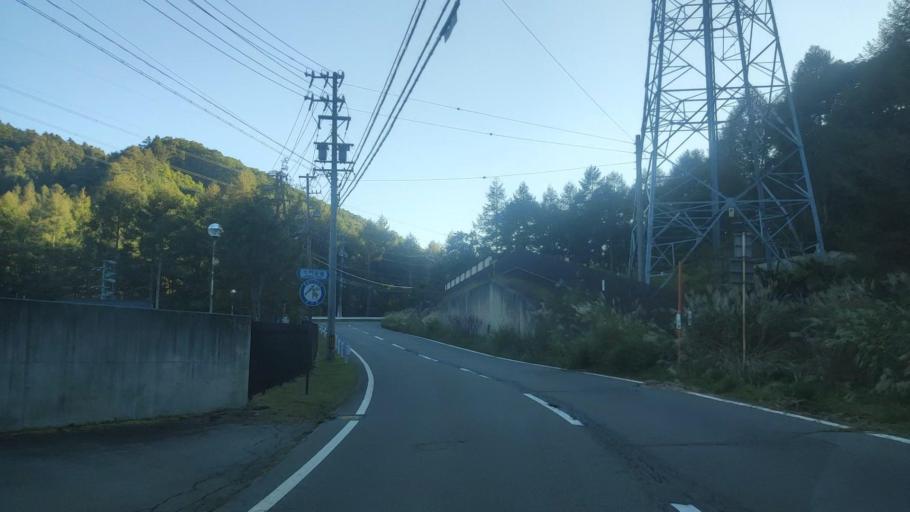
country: JP
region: Nagano
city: Suwa
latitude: 36.1403
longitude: 138.2338
